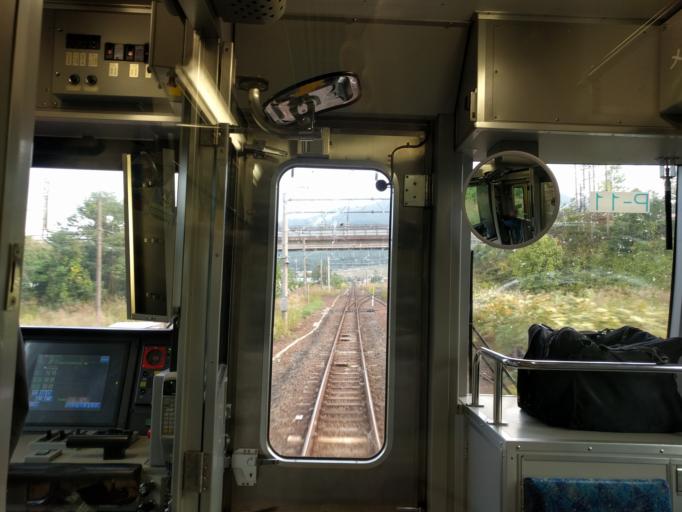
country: JP
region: Fukushima
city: Inawashiro
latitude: 37.5541
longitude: 139.9934
